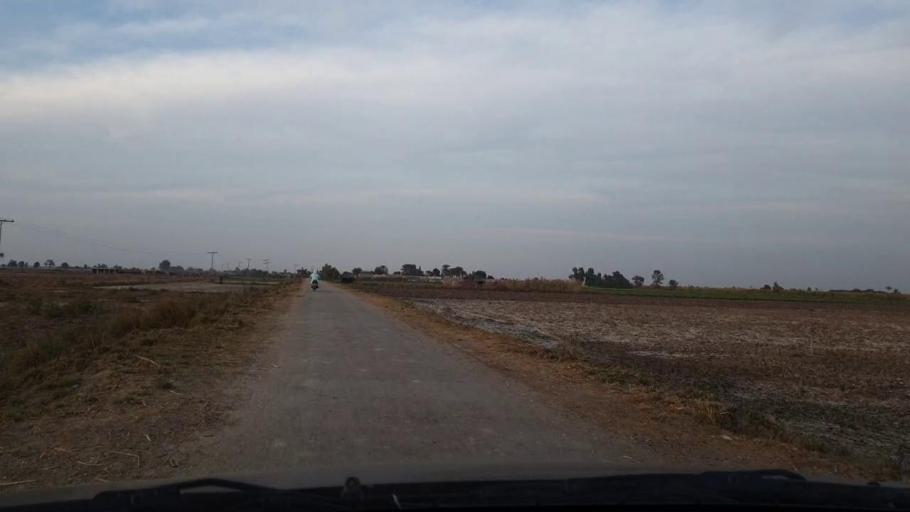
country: PK
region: Sindh
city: Khadro
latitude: 26.1334
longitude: 68.7571
